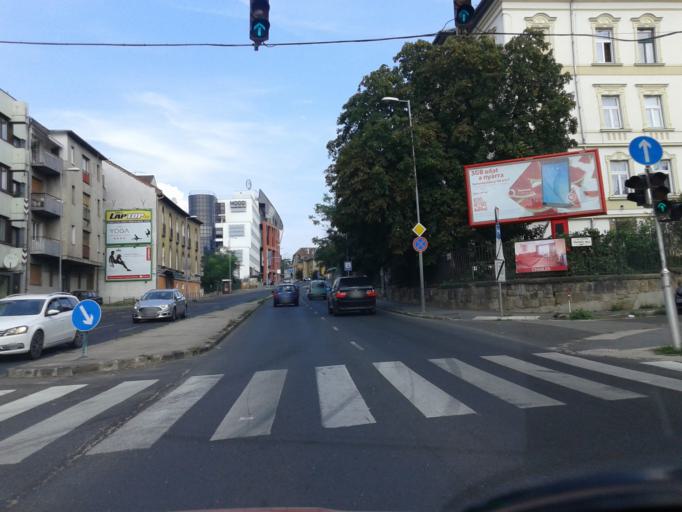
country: HU
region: Budapest
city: Budapest I. keruelet
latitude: 47.4885
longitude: 19.0314
